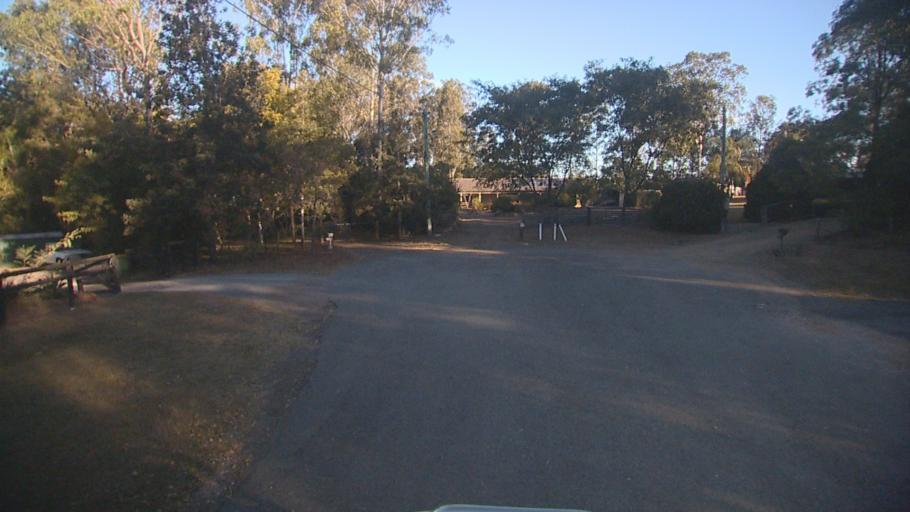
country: AU
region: Queensland
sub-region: Logan
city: Cedar Vale
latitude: -27.8668
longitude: 152.9738
